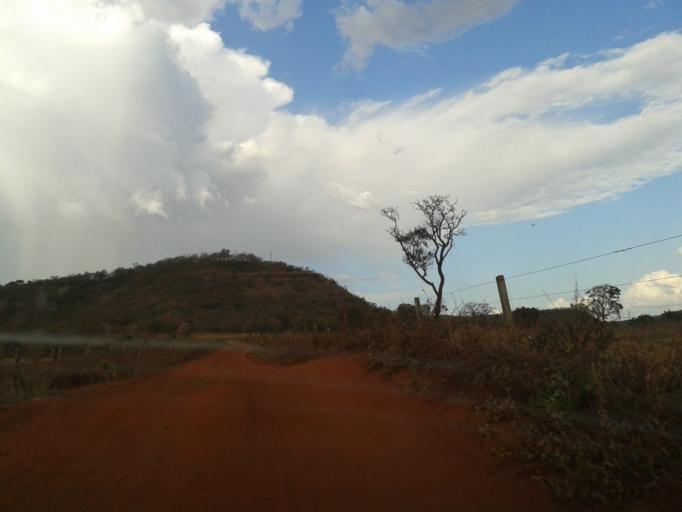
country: BR
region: Minas Gerais
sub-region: Santa Vitoria
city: Santa Vitoria
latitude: -19.2038
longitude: -49.8882
